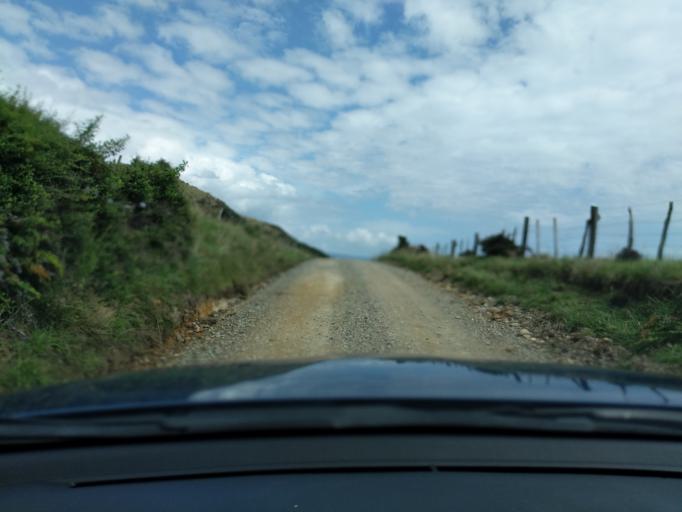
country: NZ
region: Tasman
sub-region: Tasman District
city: Takaka
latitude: -40.6657
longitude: 172.4077
